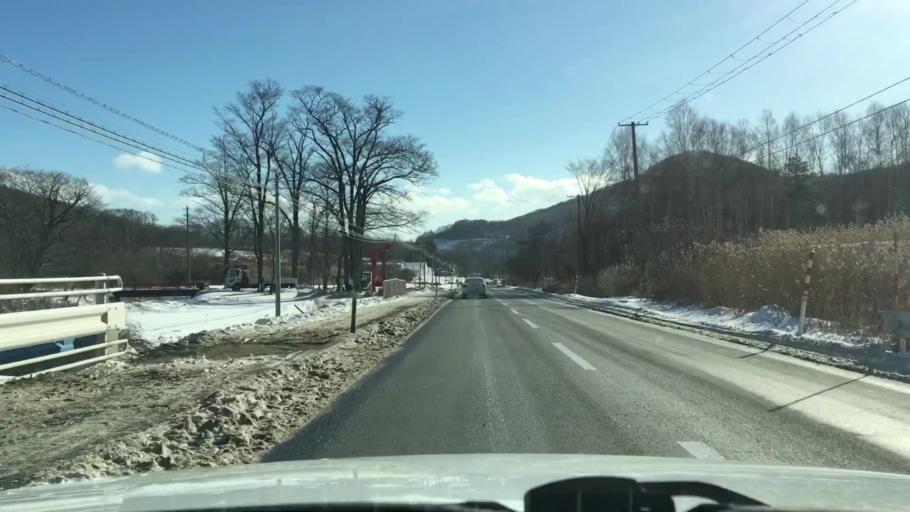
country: JP
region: Iwate
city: Morioka-shi
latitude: 39.6453
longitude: 141.3681
